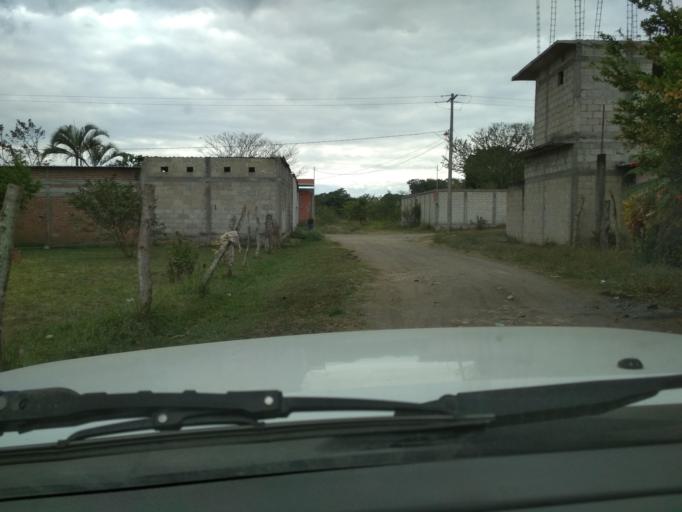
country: MX
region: Veracruz
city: El Tejar
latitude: 19.0716
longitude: -96.1462
